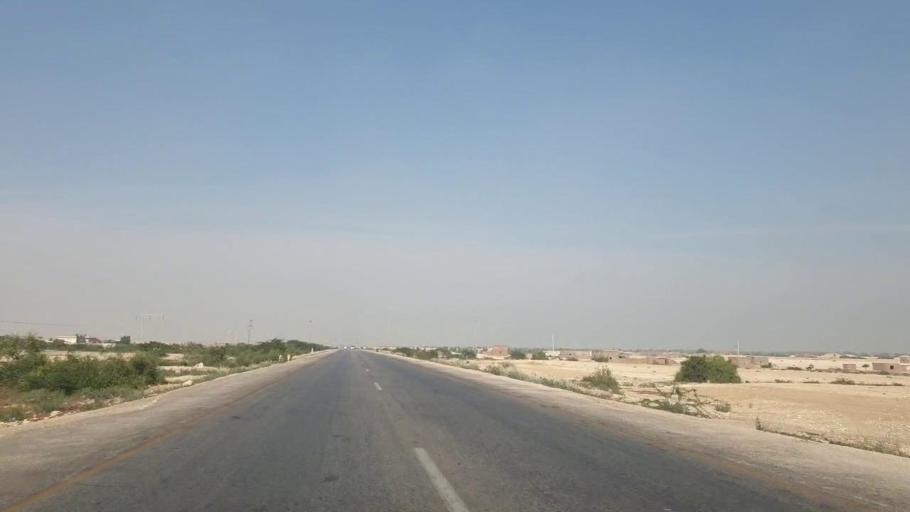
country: PK
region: Sindh
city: Hala
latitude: 25.8029
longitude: 68.2778
